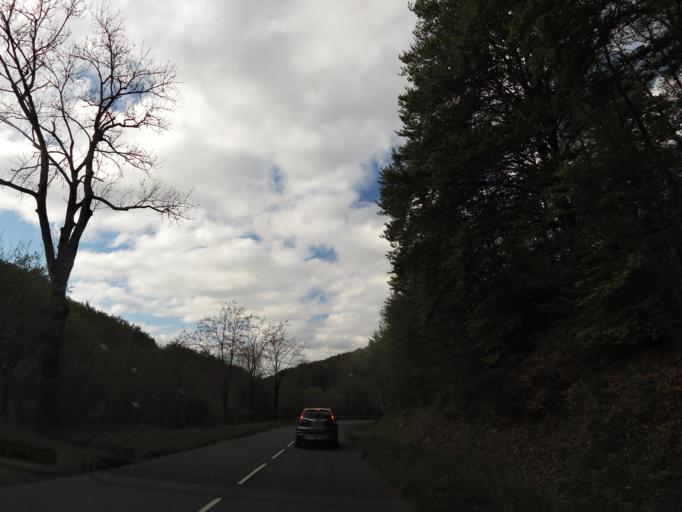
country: FR
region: Midi-Pyrenees
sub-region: Departement du Tarn
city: Soreze
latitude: 43.4171
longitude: 2.0613
